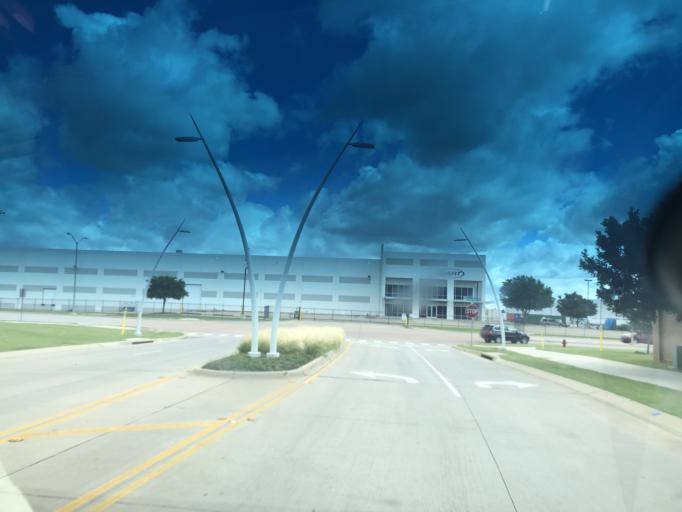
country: US
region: Texas
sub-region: Dallas County
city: Grand Prairie
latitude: 32.7049
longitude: -97.0309
